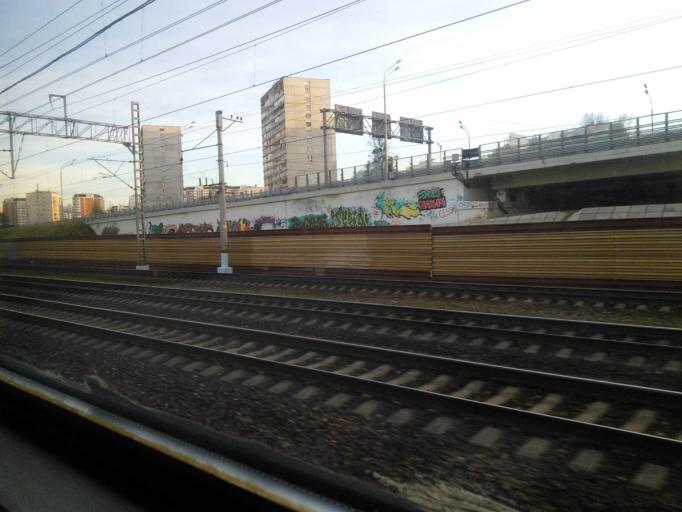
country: RU
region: Moskovskaya
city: Levoberezhnaya
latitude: 55.8783
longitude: 37.4894
